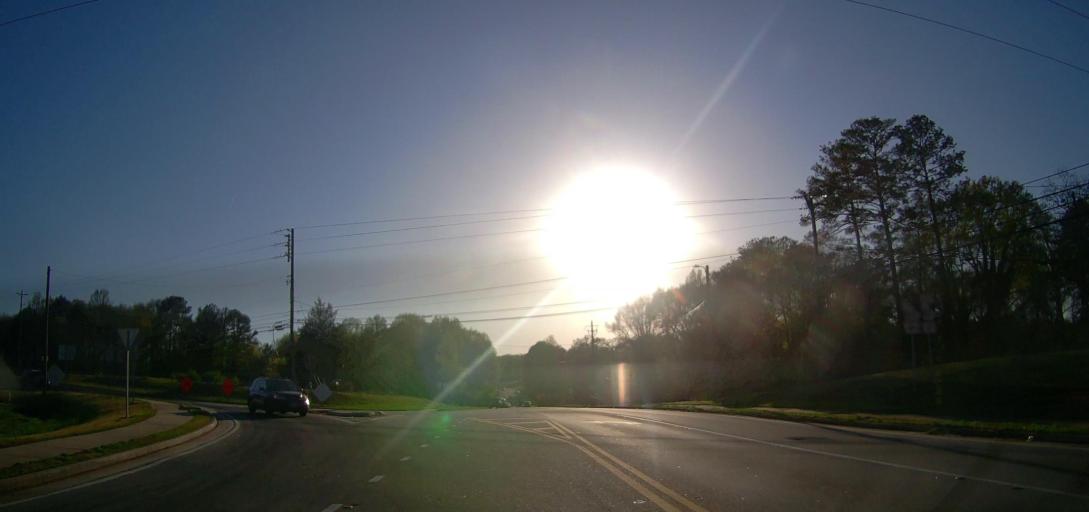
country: US
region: Georgia
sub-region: Newton County
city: Porterdale
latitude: 33.5653
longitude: -83.9035
